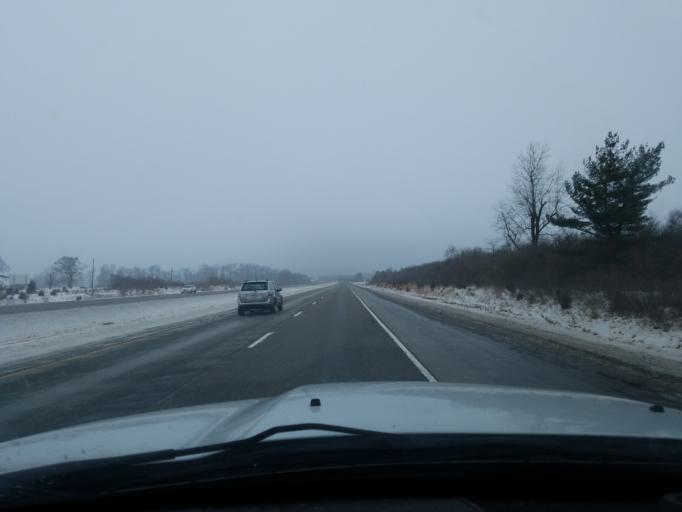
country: US
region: Indiana
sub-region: Fulton County
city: Rochester
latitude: 40.9981
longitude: -86.1676
